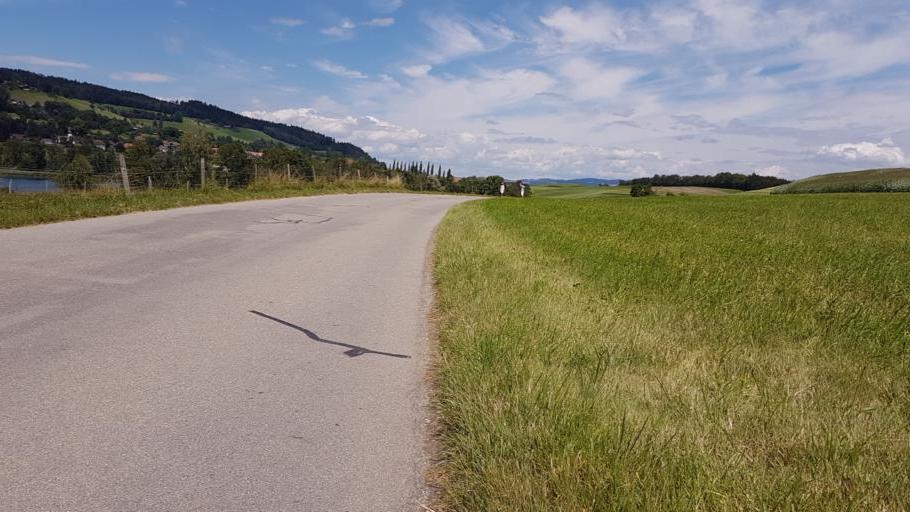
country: CH
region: Bern
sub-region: Bern-Mittelland District
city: Niederwichtrach
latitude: 46.8268
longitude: 7.5497
